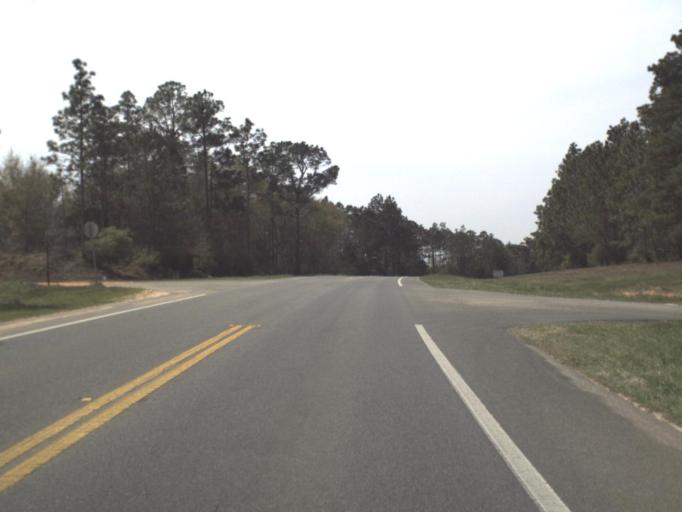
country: US
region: Florida
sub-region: Walton County
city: DeFuniak Springs
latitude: 30.7237
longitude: -85.9781
